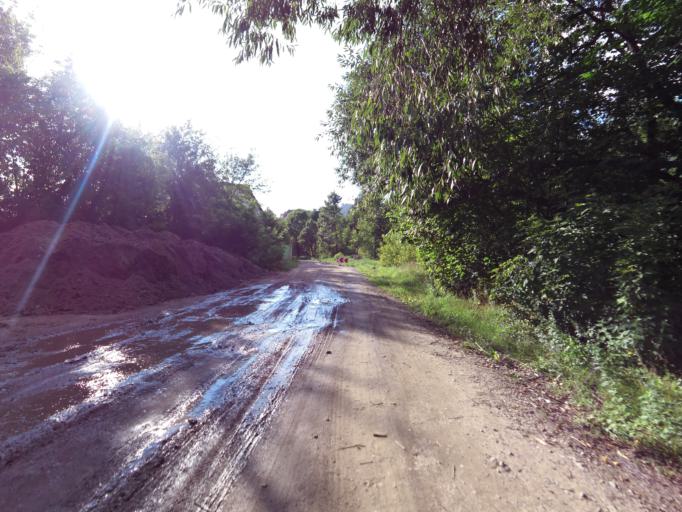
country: LT
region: Vilnius County
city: Rasos
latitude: 54.6803
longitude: 25.3027
